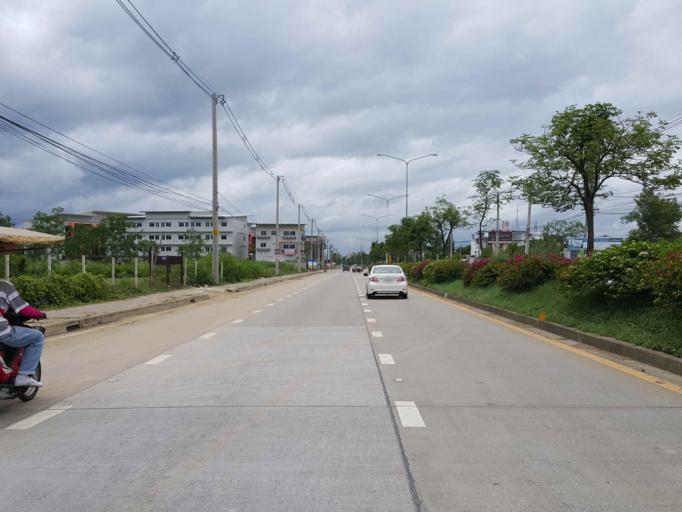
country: TH
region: Chiang Mai
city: San Sai
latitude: 18.8390
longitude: 98.9998
